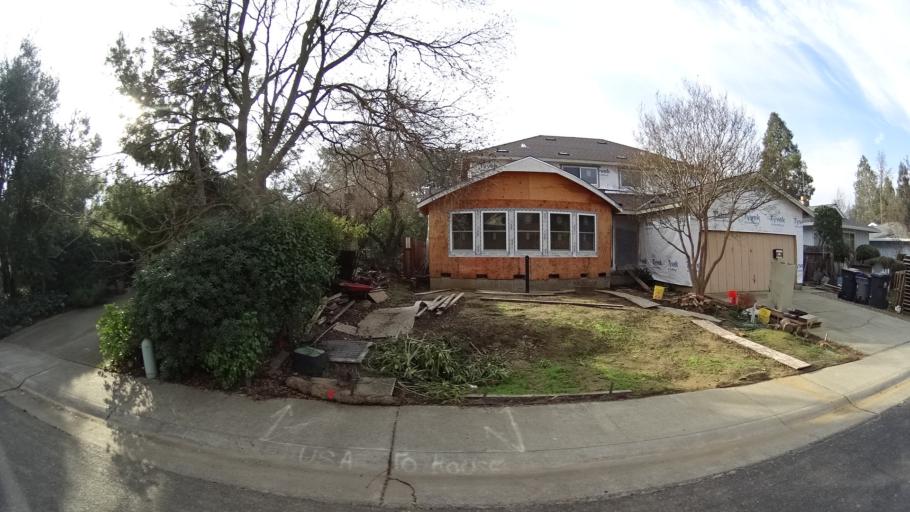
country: US
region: California
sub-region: Yolo County
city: Davis
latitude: 38.5591
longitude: -121.7140
